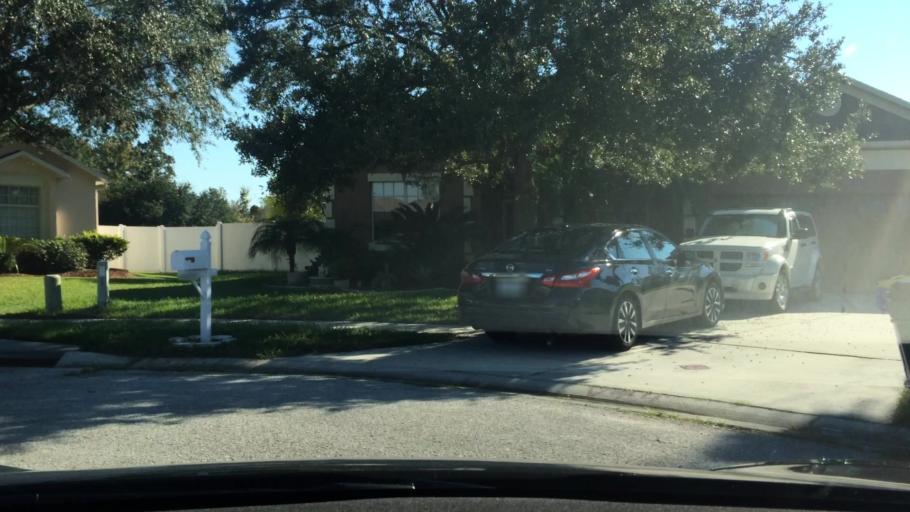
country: US
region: Florida
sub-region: Pasco County
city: Land O' Lakes
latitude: 28.2083
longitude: -82.3953
